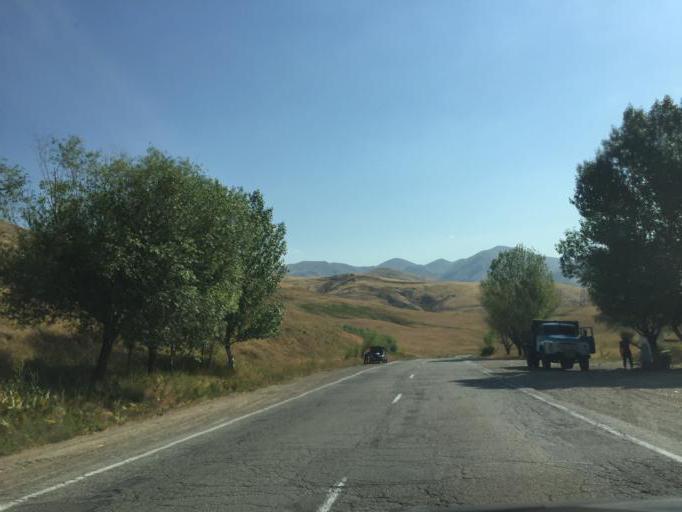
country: AM
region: Ararat
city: Zangakatun
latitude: 39.8188
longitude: 44.9981
